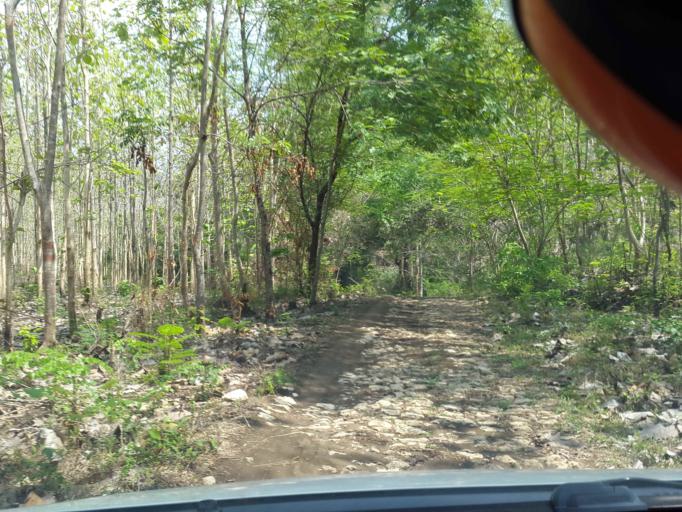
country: ID
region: East Java
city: Ponorogo
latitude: -7.8244
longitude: 111.3239
